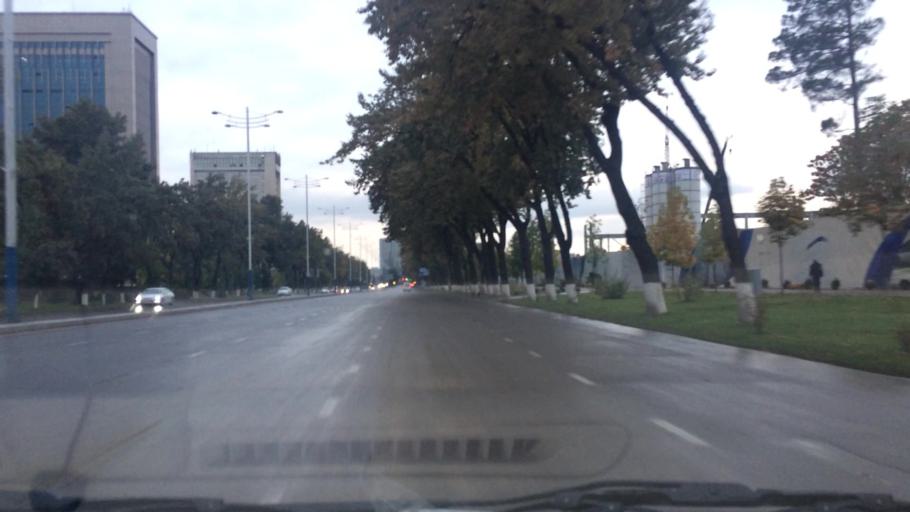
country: UZ
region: Toshkent Shahri
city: Tashkent
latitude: 41.3115
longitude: 69.2518
